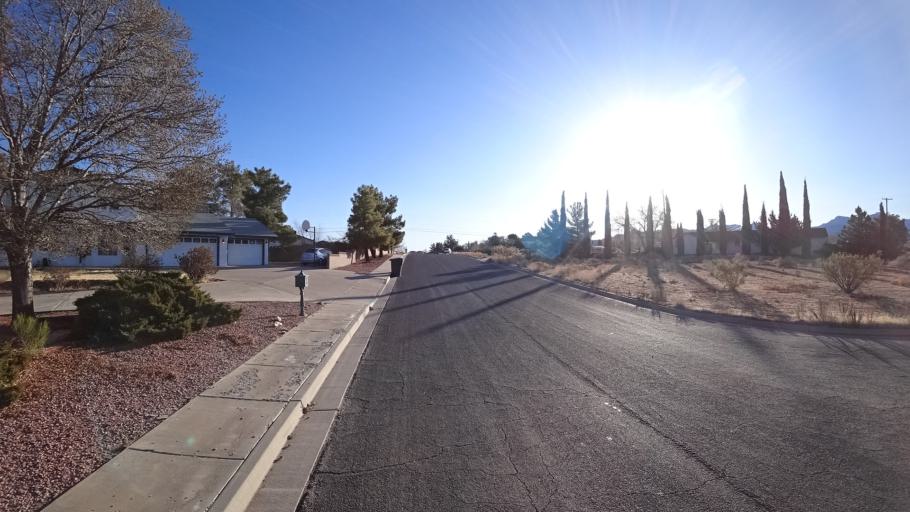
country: US
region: Arizona
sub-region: Mohave County
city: Kingman
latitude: 35.1991
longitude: -114.0067
